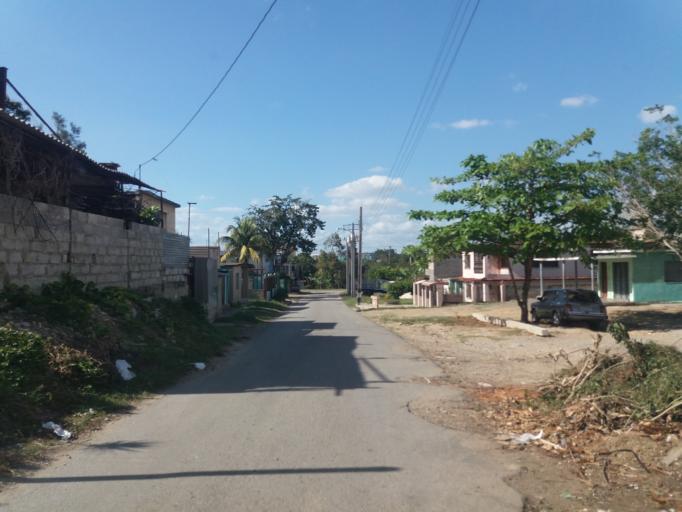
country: CU
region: Cienfuegos
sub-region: Municipio de Cienfuegos
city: Cienfuegos
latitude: 22.1545
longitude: -80.4322
